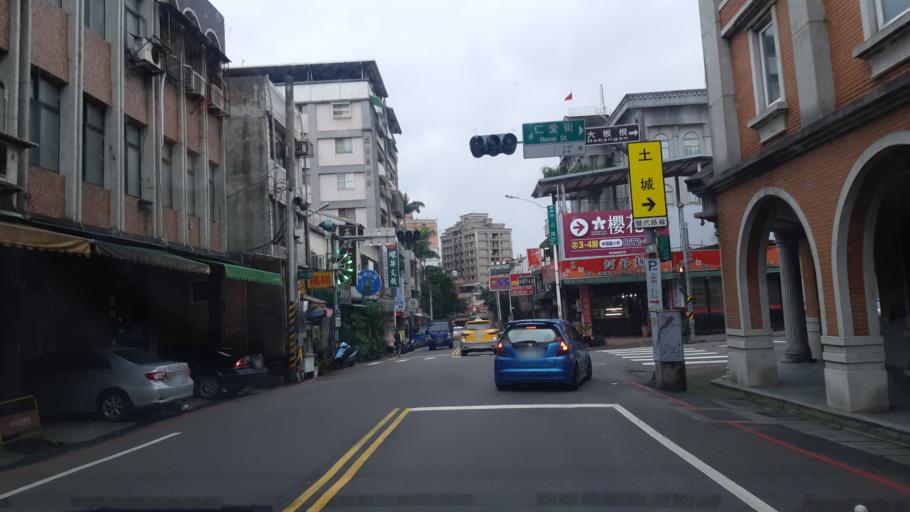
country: TW
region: Taiwan
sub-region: Taoyuan
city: Taoyuan
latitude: 24.9345
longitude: 121.3681
